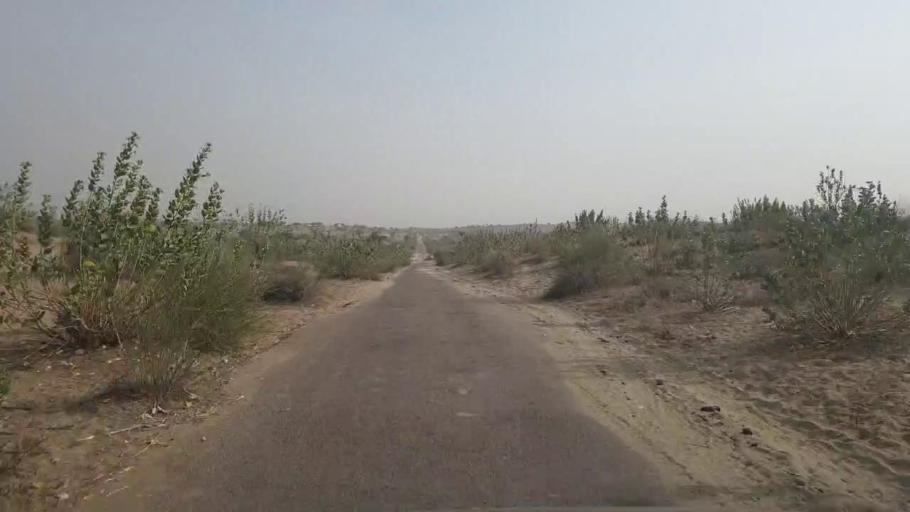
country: PK
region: Sindh
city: Chor
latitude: 25.5208
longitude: 69.9634
